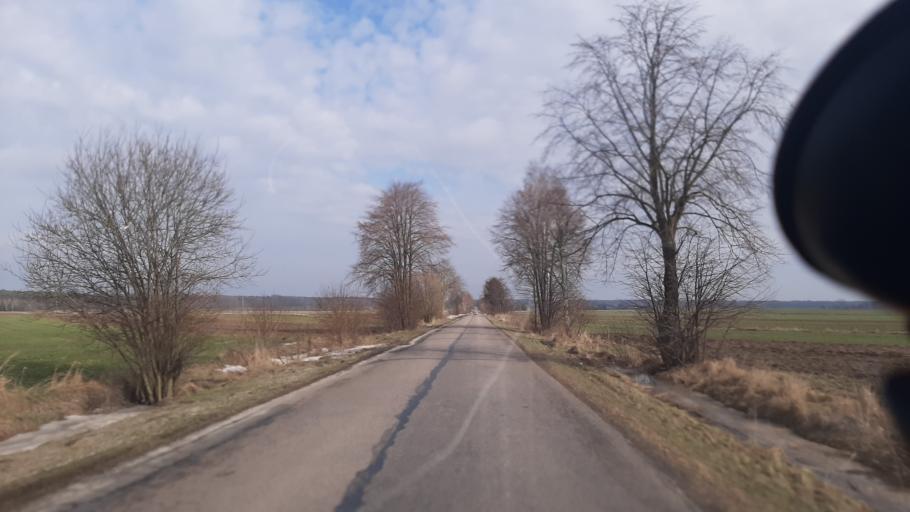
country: PL
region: Lublin Voivodeship
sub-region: Powiat lubartowski
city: Wola Sernicka
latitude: 51.4606
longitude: 22.7041
